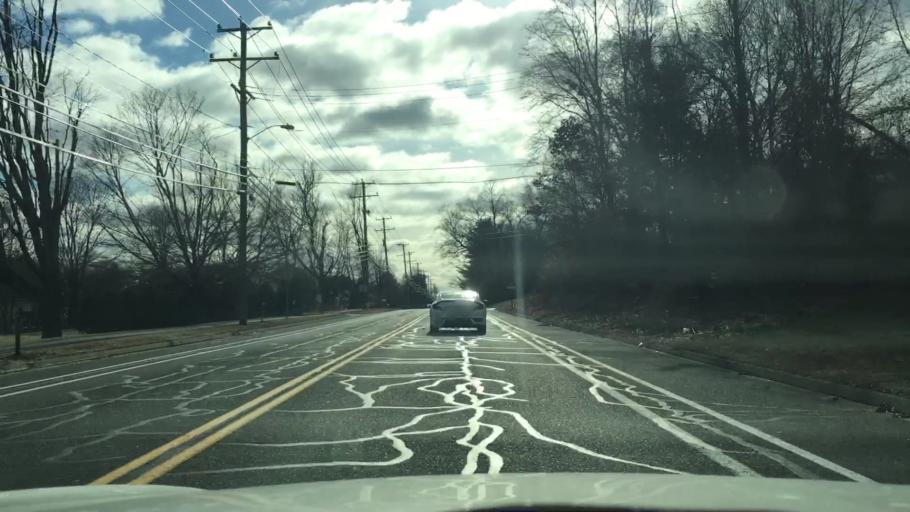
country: US
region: Massachusetts
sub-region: Hampden County
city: Agawam
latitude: 42.0579
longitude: -72.6329
